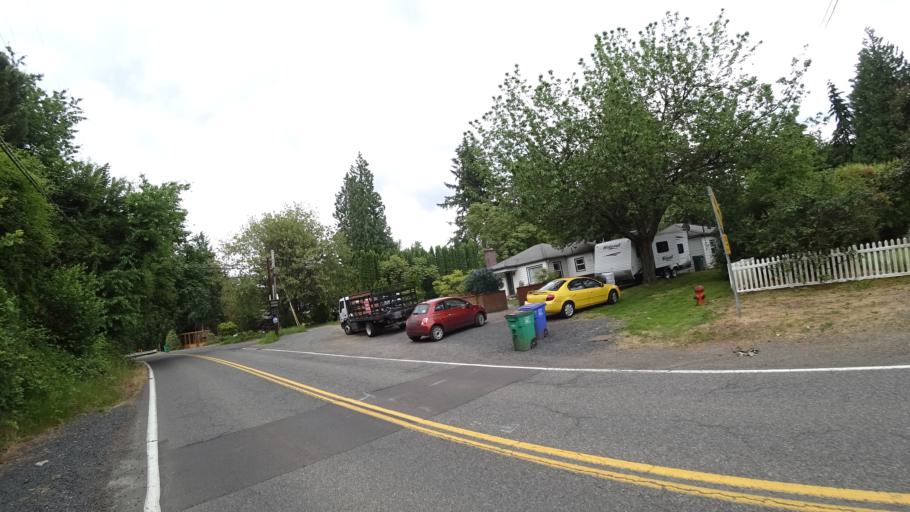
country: US
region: Oregon
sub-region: Clackamas County
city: Lake Oswego
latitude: 45.4582
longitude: -122.7004
